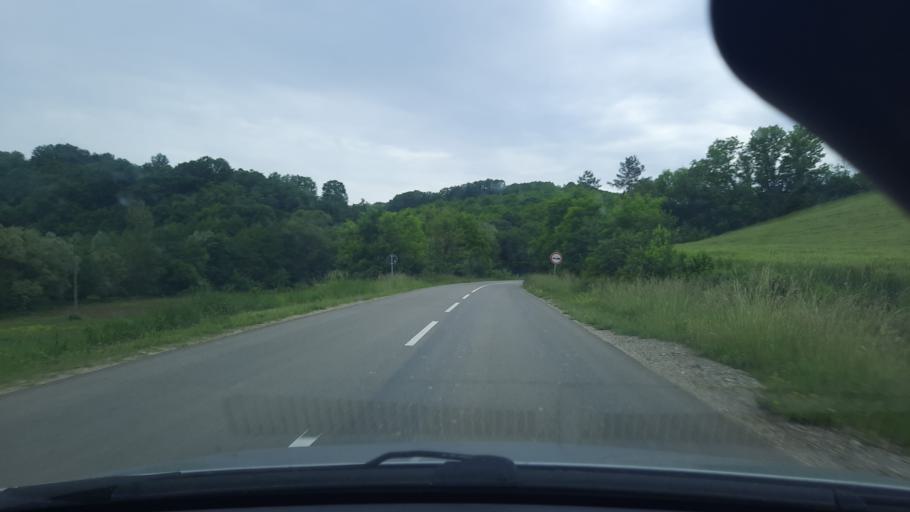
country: RS
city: Bukor
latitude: 44.5146
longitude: 19.5101
